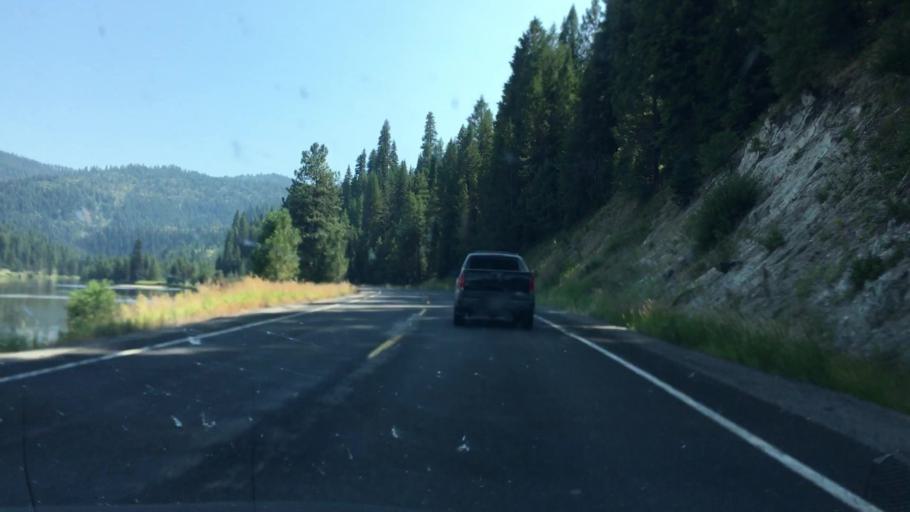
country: US
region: Idaho
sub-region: Valley County
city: Cascade
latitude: 44.2844
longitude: -116.0809
